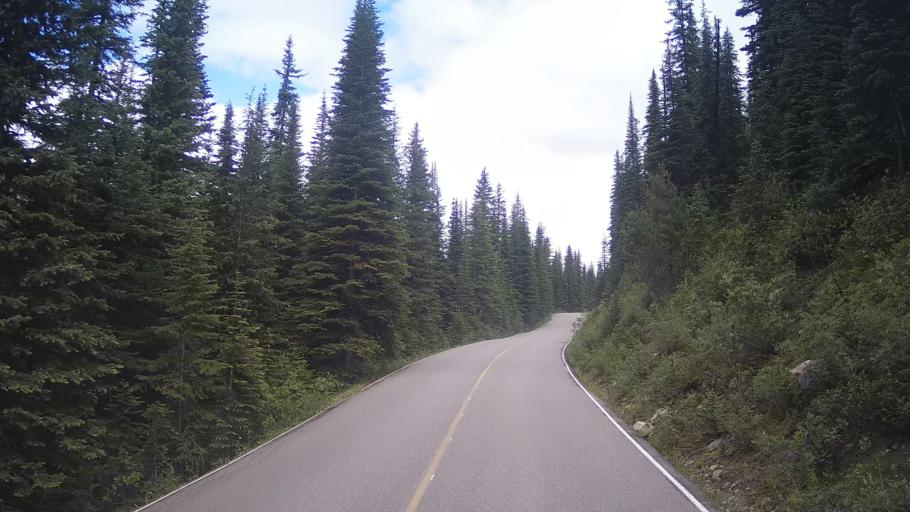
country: CA
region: Alberta
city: Jasper Park Lodge
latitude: 52.6909
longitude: -118.0571
